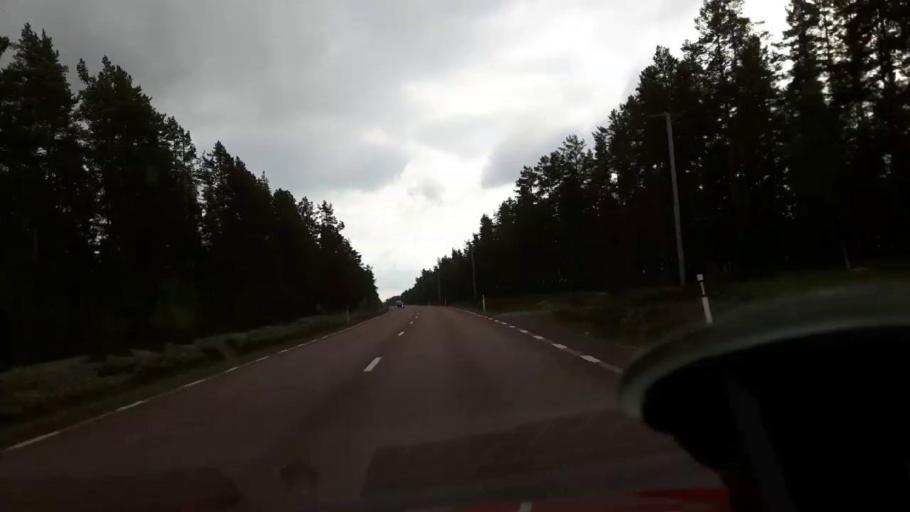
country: SE
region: Gaevleborg
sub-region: Soderhamns Kommun
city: Ljusne
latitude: 61.1086
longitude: 16.9382
